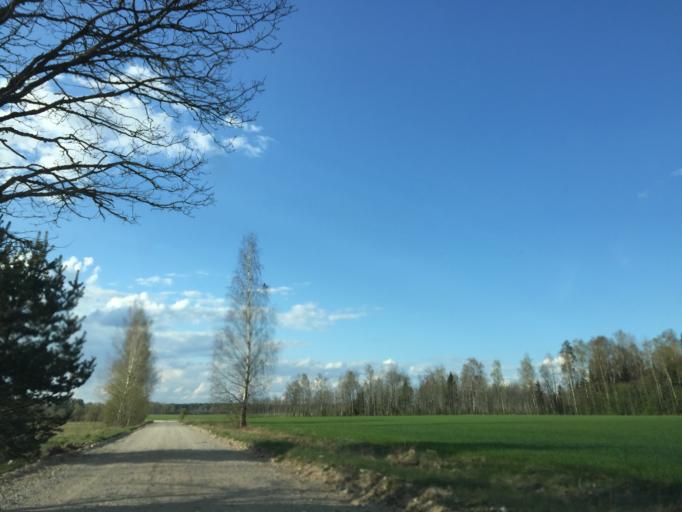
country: LV
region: Beverina
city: Murmuiza
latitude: 57.3840
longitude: 25.4853
